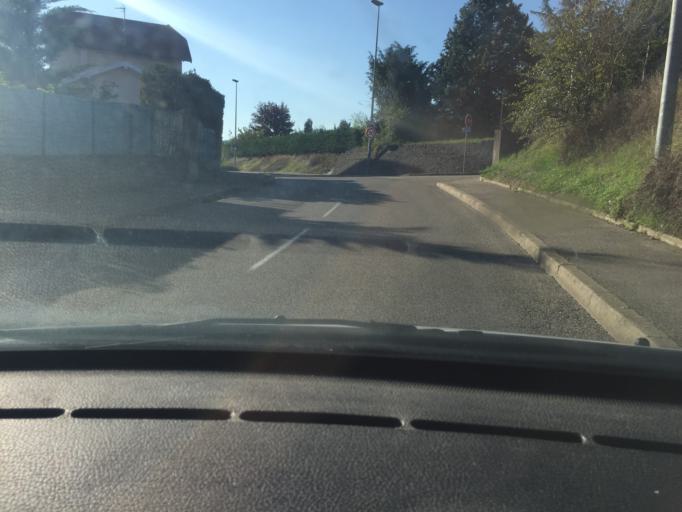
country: FR
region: Rhone-Alpes
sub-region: Departement de l'Ain
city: Saint-Maurice-de-Beynost
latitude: 45.8316
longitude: 4.9803
